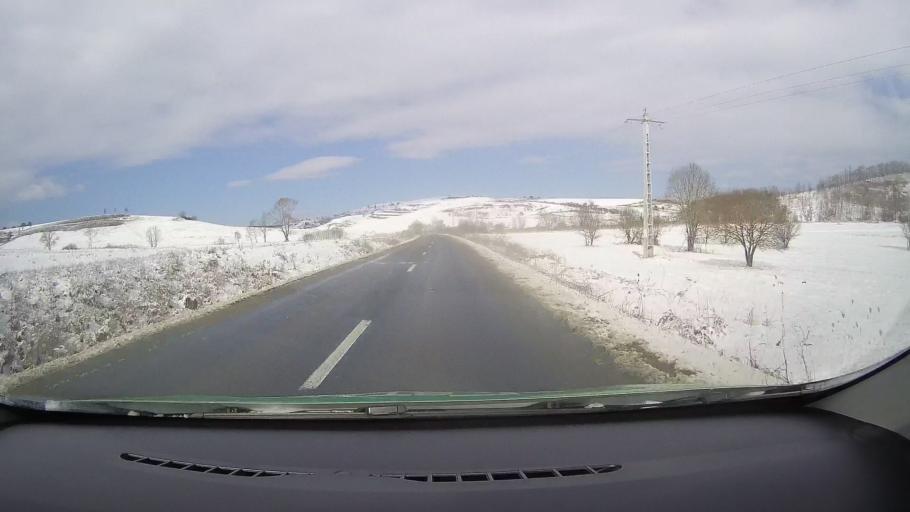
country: RO
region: Sibiu
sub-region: Comuna Altina
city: Altina
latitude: 45.9727
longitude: 24.4662
